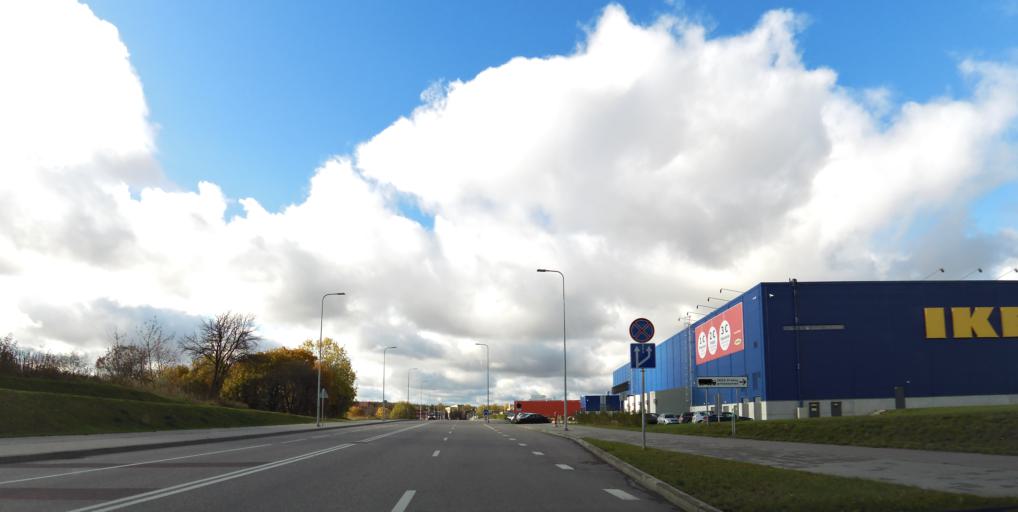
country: LT
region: Vilnius County
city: Naujamiestis
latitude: 54.6501
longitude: 25.2817
